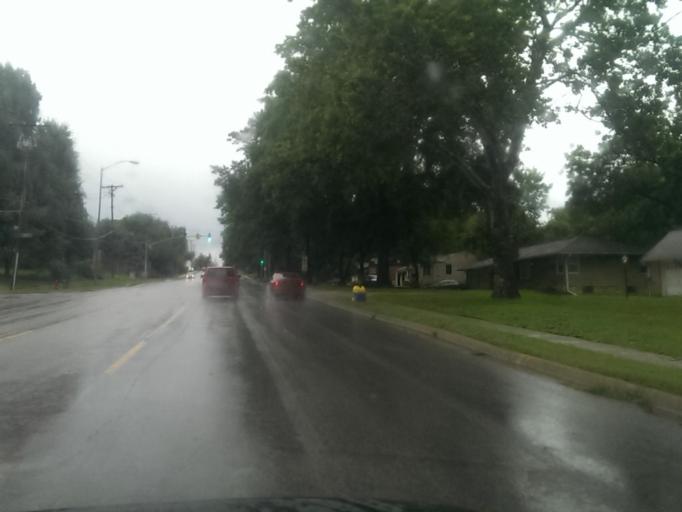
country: US
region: Kansas
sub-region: Johnson County
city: Leawood
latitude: 38.9301
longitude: -94.5829
